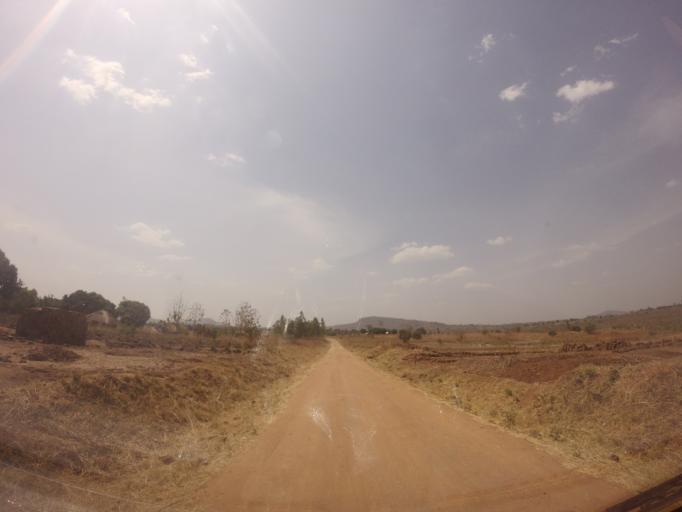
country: UG
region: Northern Region
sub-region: Arua District
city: Arua
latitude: 2.9106
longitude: 31.0514
